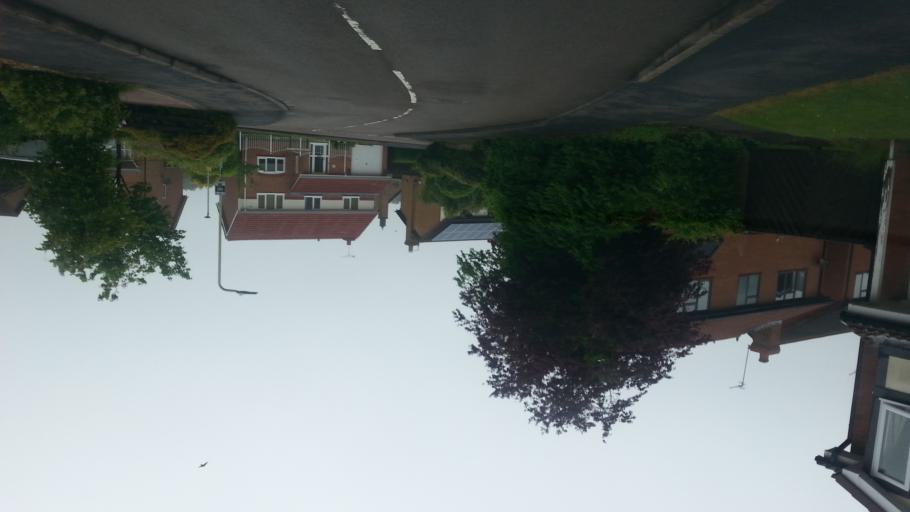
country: GB
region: England
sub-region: Leicestershire
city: Great Glen
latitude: 52.5928
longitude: -1.0544
